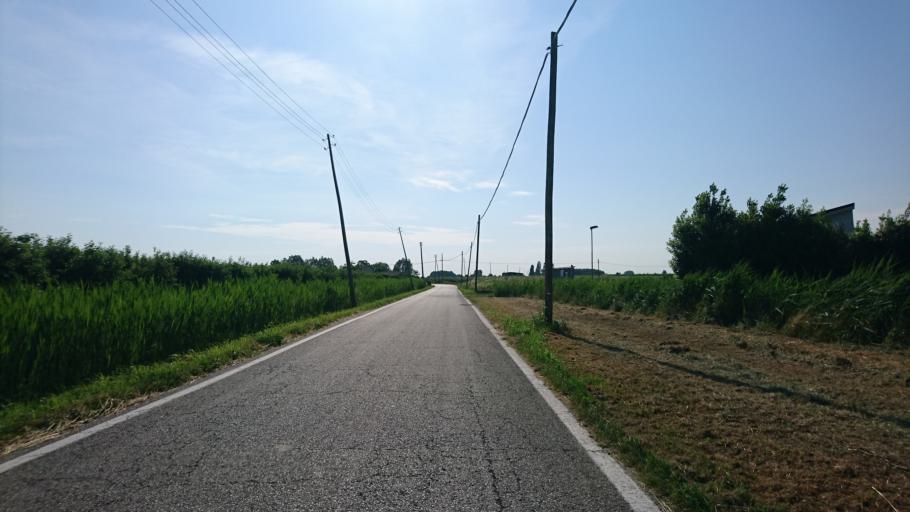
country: IT
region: Veneto
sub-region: Provincia di Verona
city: Villa Bartolomea
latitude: 45.1668
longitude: 11.3694
